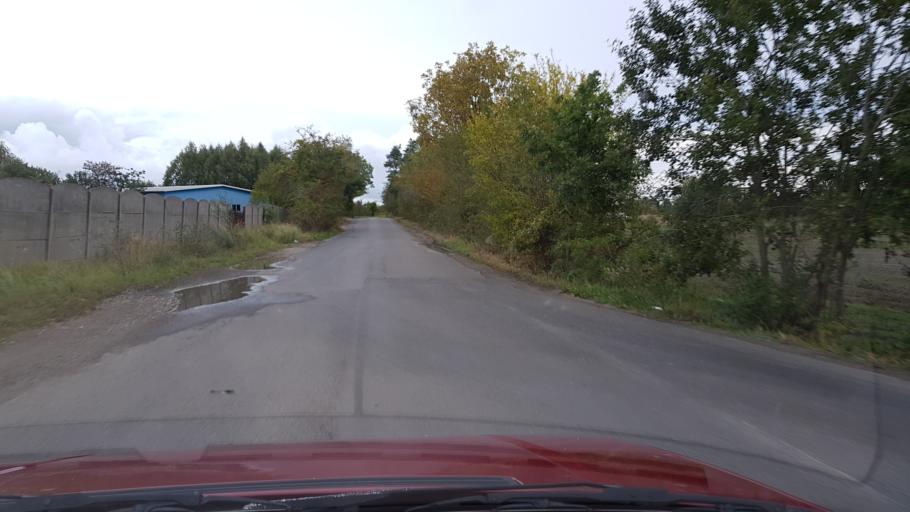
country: PL
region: West Pomeranian Voivodeship
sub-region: Koszalin
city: Koszalin
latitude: 54.1782
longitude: 16.1473
